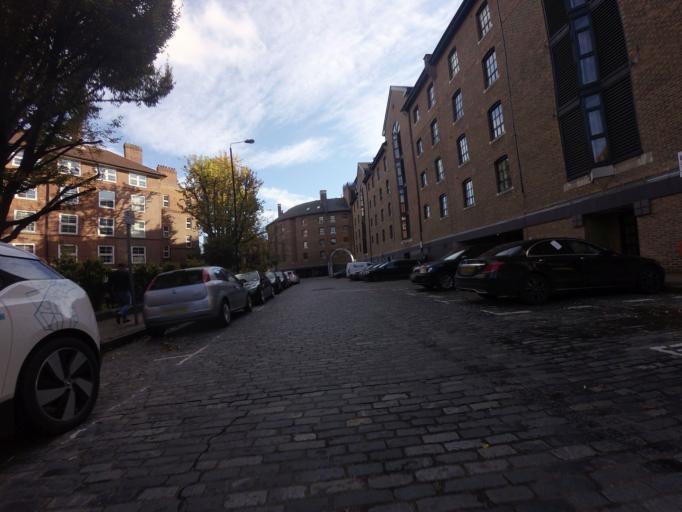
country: GB
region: England
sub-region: Greater London
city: City of London
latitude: 51.5053
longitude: -0.0698
